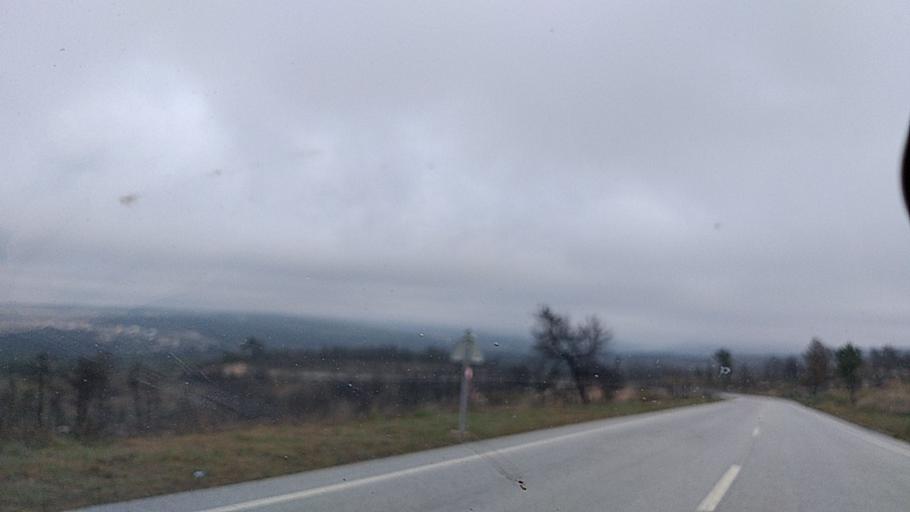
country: PT
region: Guarda
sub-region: Fornos de Algodres
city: Fornos de Algodres
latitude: 40.7033
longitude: -7.4838
